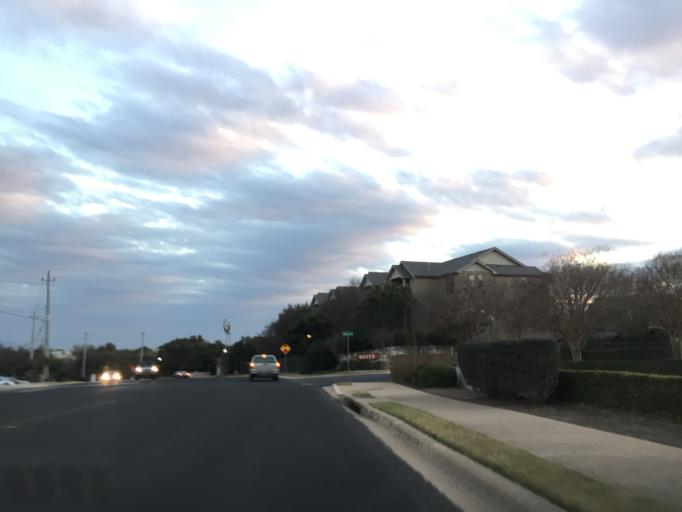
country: US
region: Texas
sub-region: Williamson County
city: Jollyville
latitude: 30.4334
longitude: -97.7390
